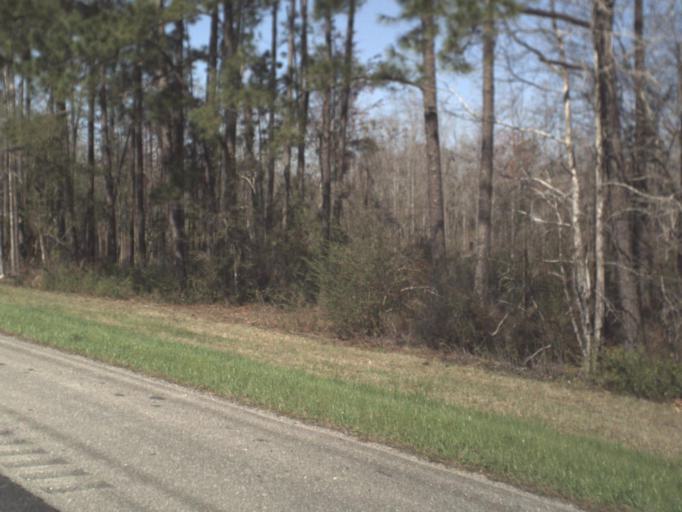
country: US
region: Florida
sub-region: Washington County
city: Chipley
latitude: 30.7466
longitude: -85.4338
